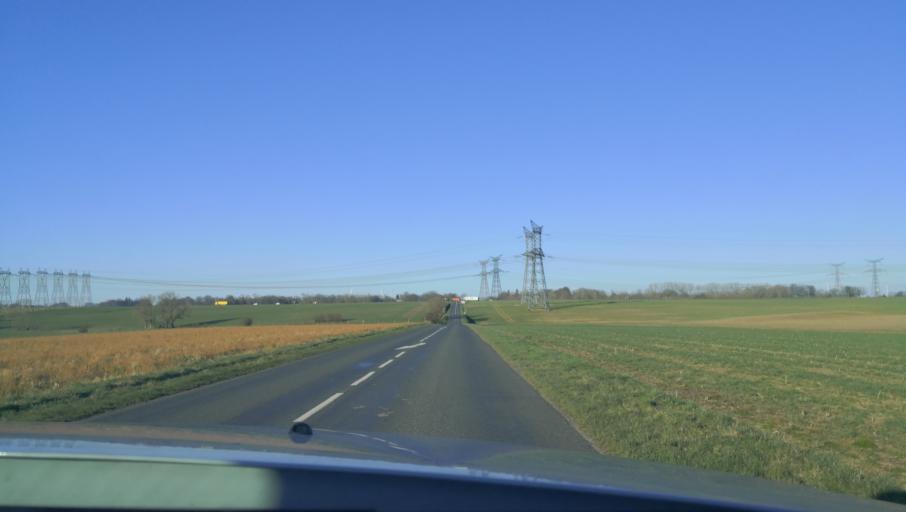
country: FR
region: Haute-Normandie
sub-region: Departement de la Seine-Maritime
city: Totes
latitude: 49.6507
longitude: 1.0165
